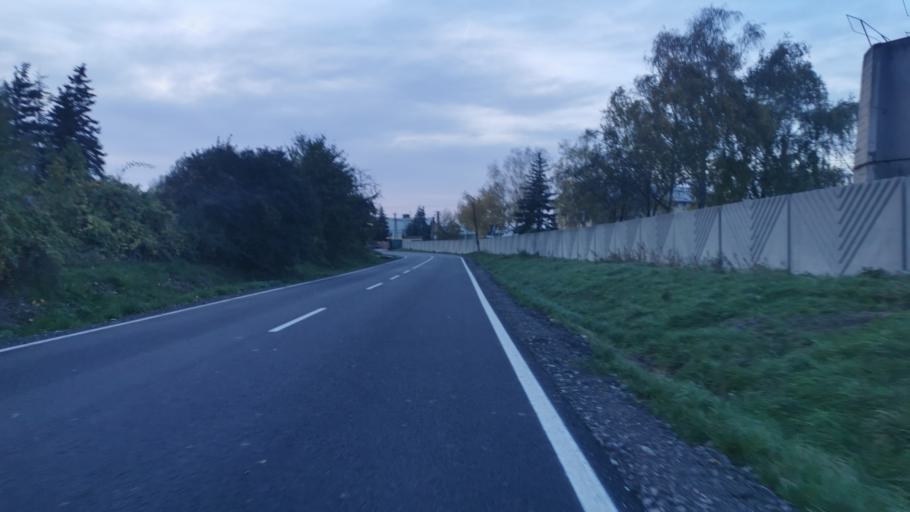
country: CZ
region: South Moravian
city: Sudomerice
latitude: 48.8470
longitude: 17.2534
